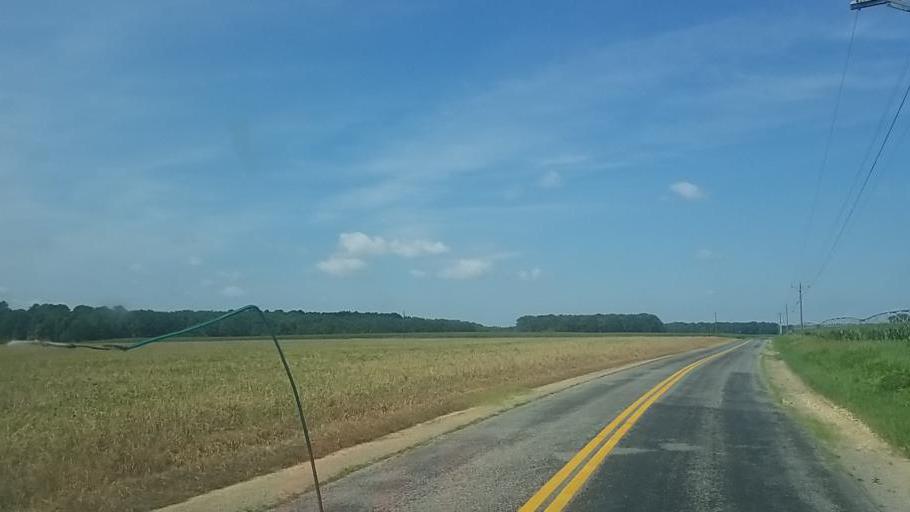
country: US
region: Maryland
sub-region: Caroline County
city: Denton
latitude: 38.8724
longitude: -75.7543
